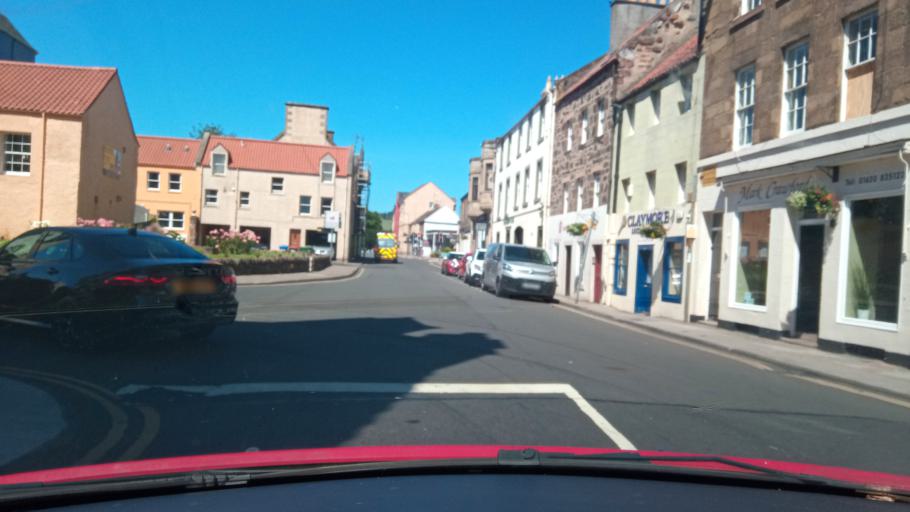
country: GB
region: Scotland
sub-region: East Lothian
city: Haddington
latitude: 55.9552
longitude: -2.7749
